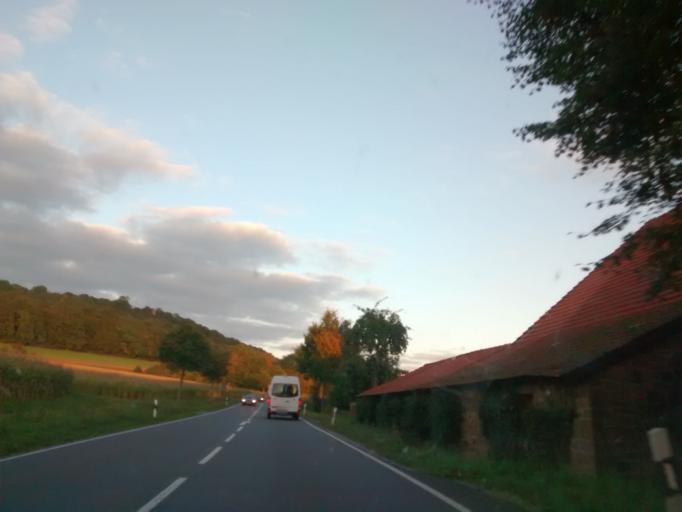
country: DE
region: North Rhine-Westphalia
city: Borgholzhausen
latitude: 52.0820
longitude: 8.2858
